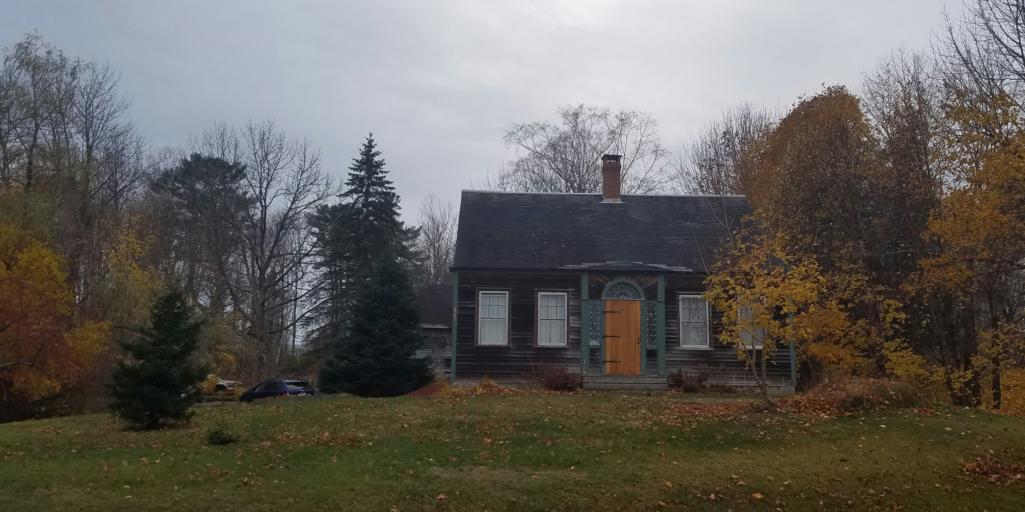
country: US
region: Maine
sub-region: Waldo County
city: Belfast
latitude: 44.4367
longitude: -69.0252
